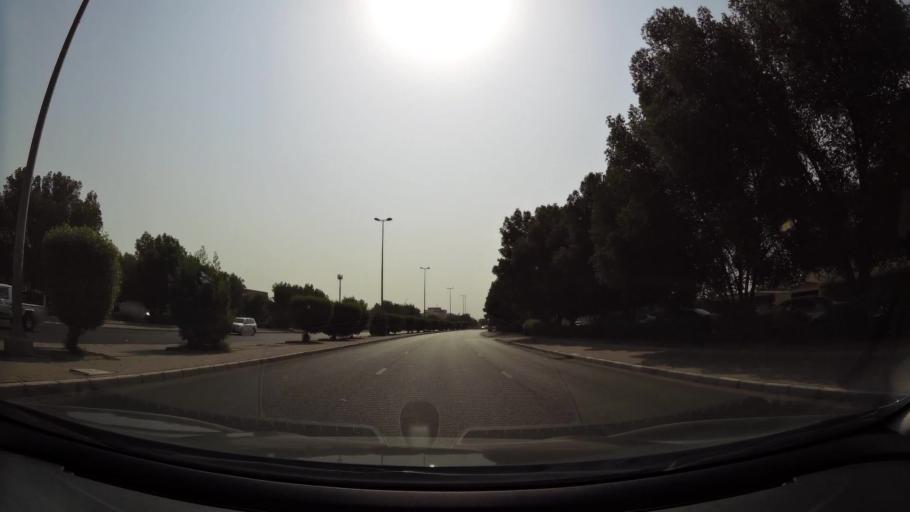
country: KW
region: Al Asimah
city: Ar Rabiyah
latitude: 29.2836
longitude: 47.8853
